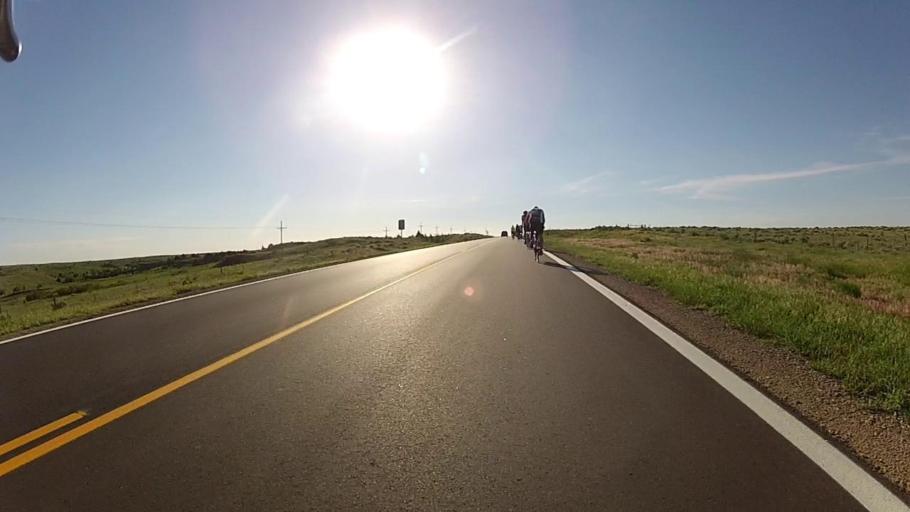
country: US
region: Kansas
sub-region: Comanche County
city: Coldwater
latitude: 37.2805
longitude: -99.0215
